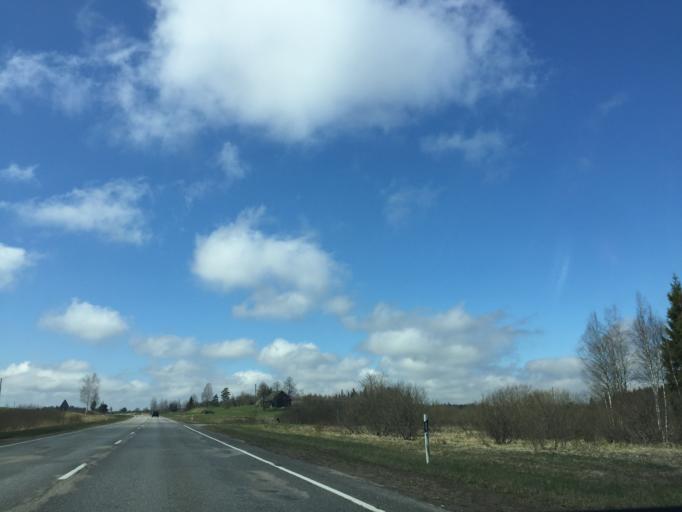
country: LV
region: Apes Novads
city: Ape
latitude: 57.4984
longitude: 26.5956
